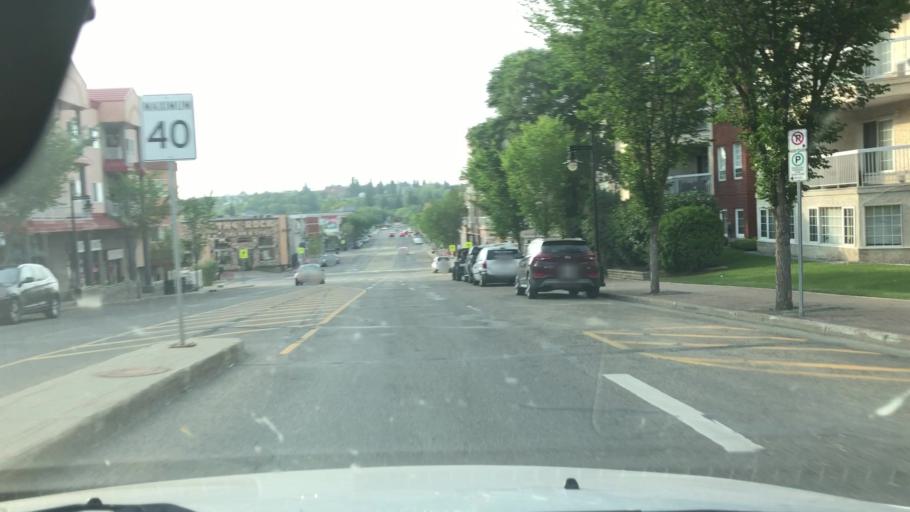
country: CA
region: Alberta
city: St. Albert
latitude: 53.6324
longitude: -113.6238
